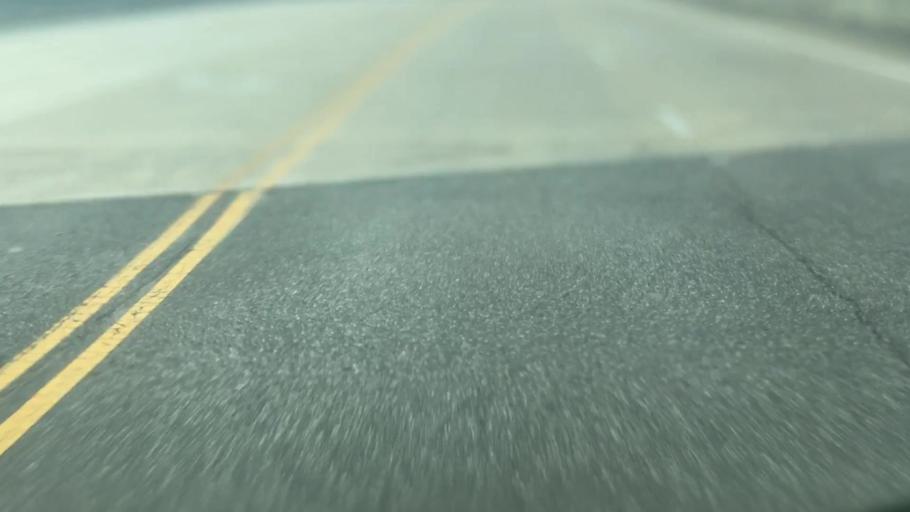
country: US
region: Alabama
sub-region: Walker County
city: Jasper
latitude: 33.8153
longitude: -87.2331
